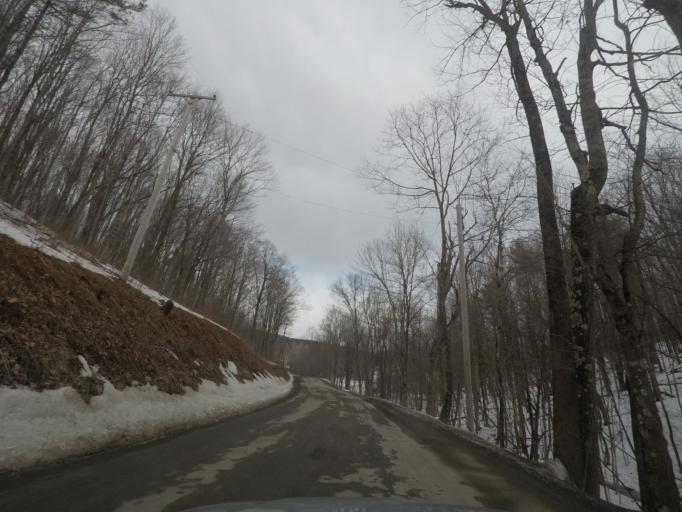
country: US
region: New York
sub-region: Saratoga County
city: Waterford
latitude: 42.7781
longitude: -73.6116
